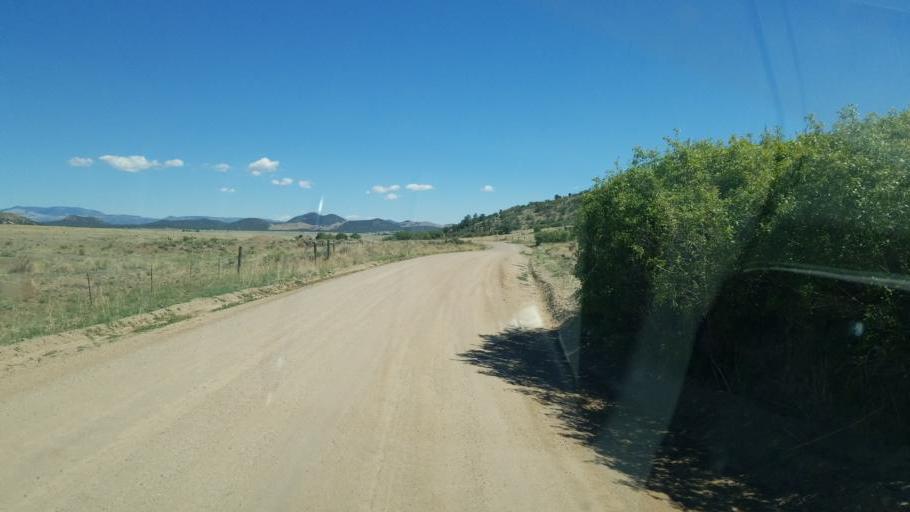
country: US
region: Colorado
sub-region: Custer County
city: Westcliffe
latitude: 38.2394
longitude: -105.5020
